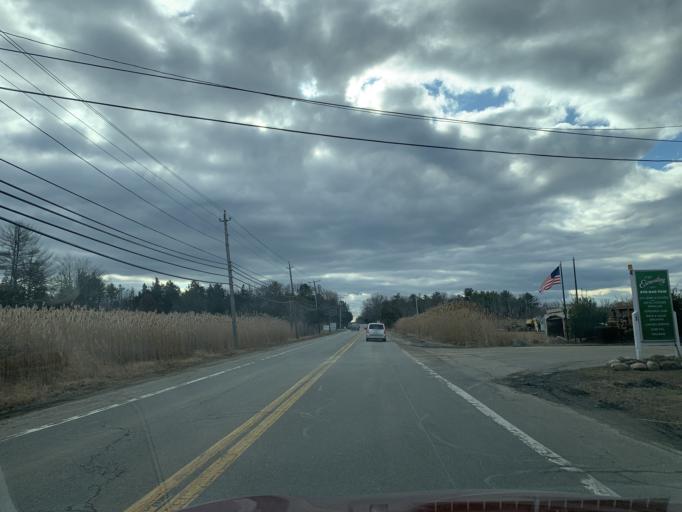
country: US
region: Massachusetts
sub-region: Essex County
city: Newburyport
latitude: 42.7830
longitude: -70.8814
